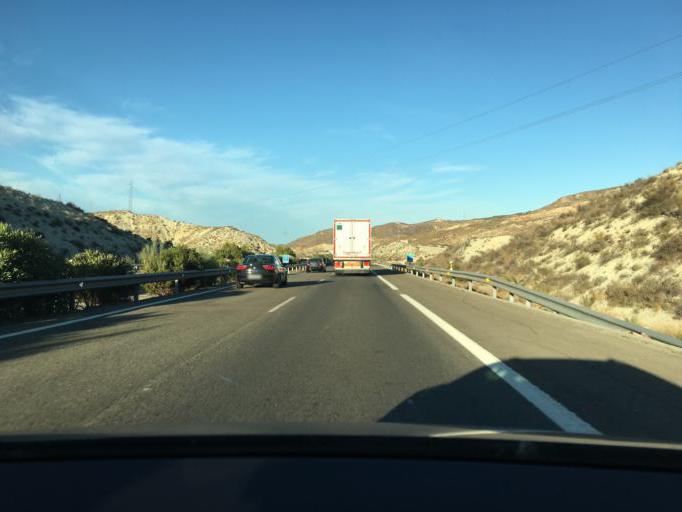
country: ES
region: Andalusia
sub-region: Provincia de Almeria
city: Sorbas
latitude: 37.0965
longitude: -2.0454
